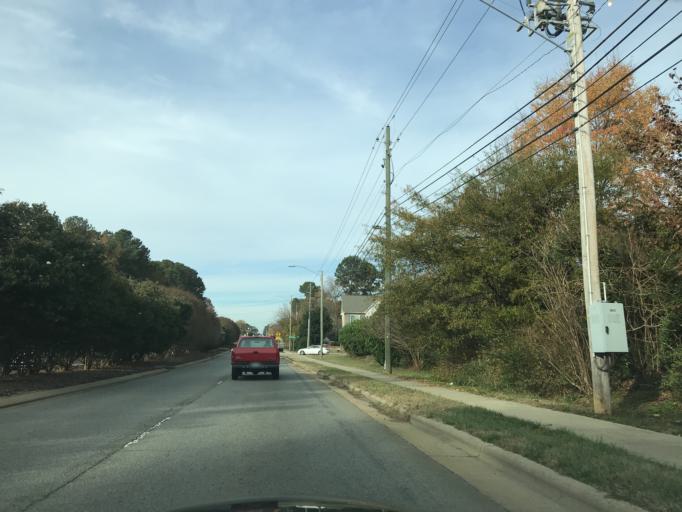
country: US
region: North Carolina
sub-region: Wake County
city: West Raleigh
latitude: 35.8802
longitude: -78.6787
